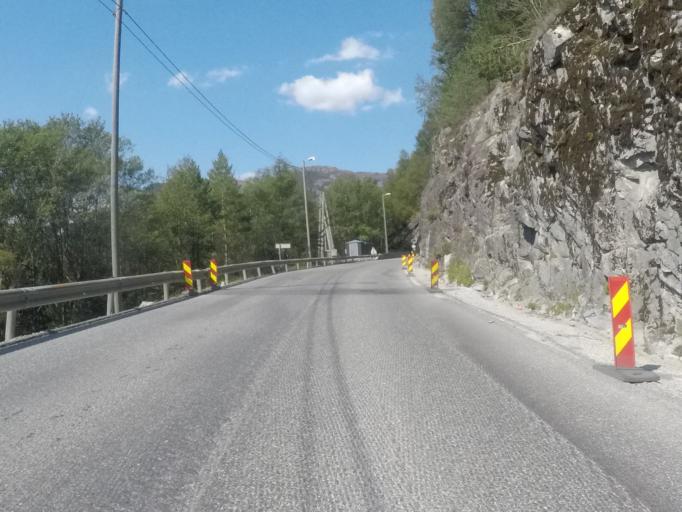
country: NO
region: Hordaland
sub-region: Modalen
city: Mo
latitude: 60.8765
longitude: 5.5592
